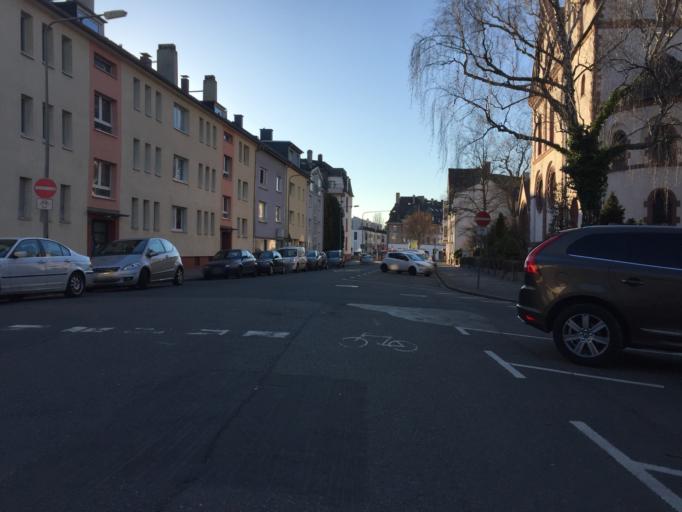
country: DE
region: Hesse
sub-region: Regierungsbezirk Darmstadt
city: Frankfurt am Main
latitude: 50.1561
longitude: 8.6596
